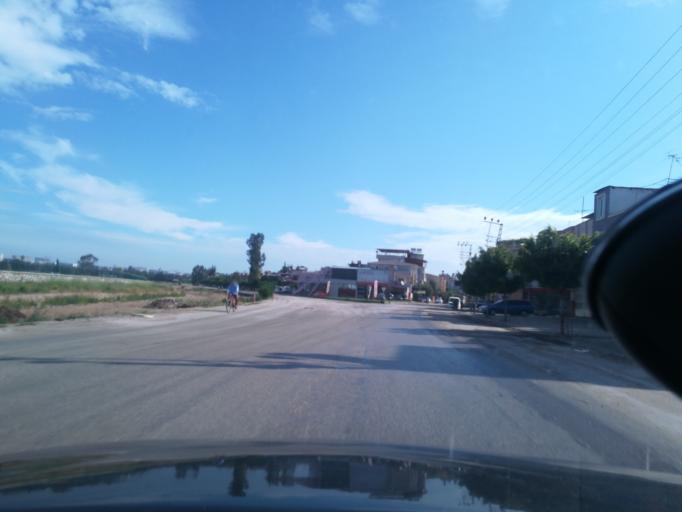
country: TR
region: Adana
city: Adana
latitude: 37.0158
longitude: 35.3621
